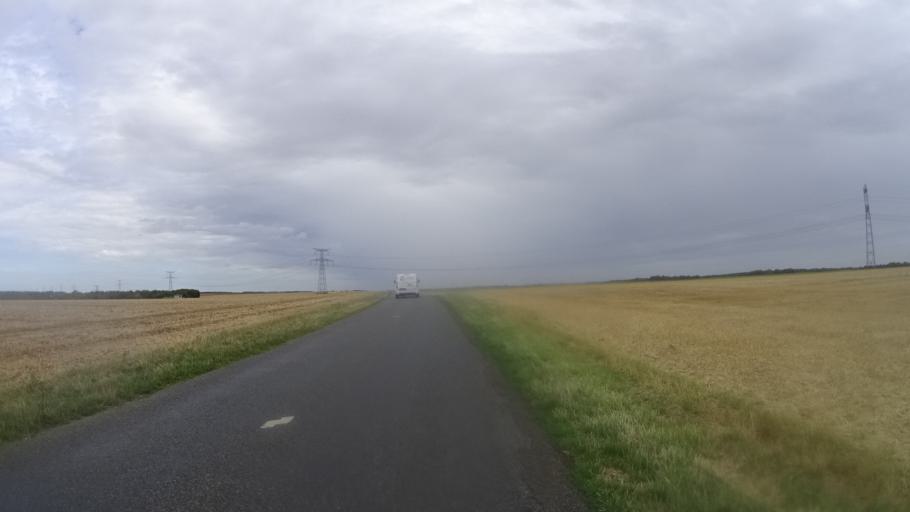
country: FR
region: Centre
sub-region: Departement du Loiret
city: Boynes
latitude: 48.1654
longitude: 2.3551
